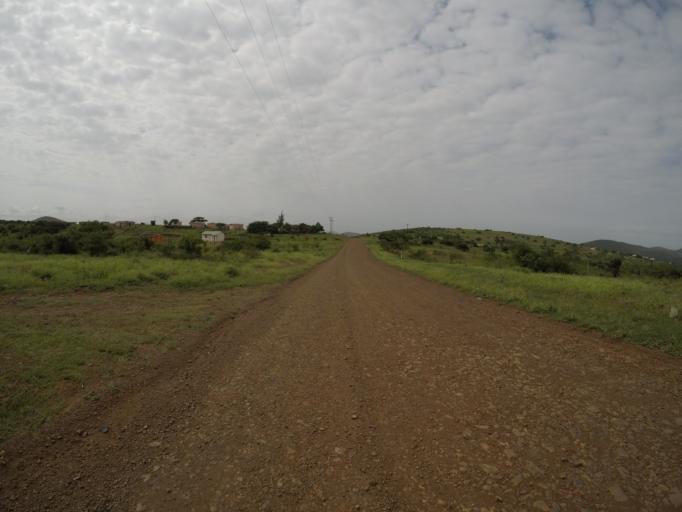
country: ZA
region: KwaZulu-Natal
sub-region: uThungulu District Municipality
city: Empangeni
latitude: -28.6177
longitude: 31.9027
